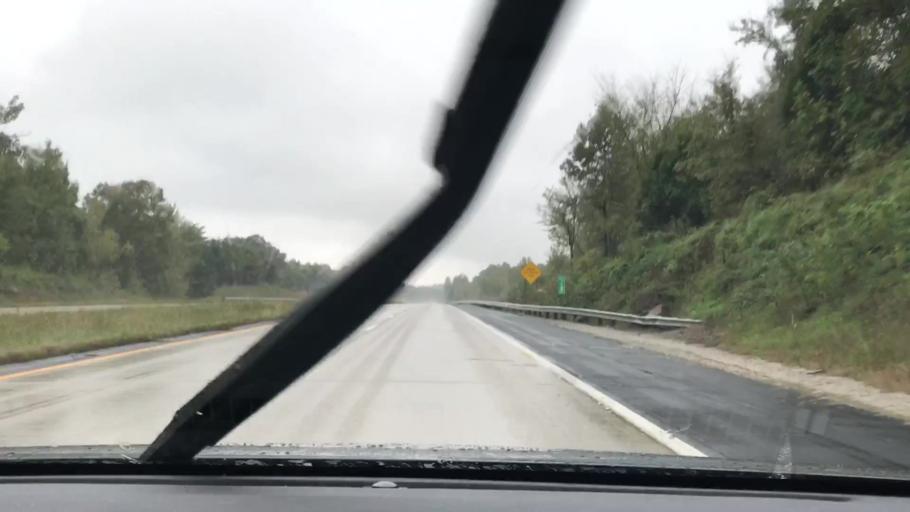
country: US
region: Kentucky
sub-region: Hopkins County
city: Nortonville
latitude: 37.1410
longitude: -87.4627
